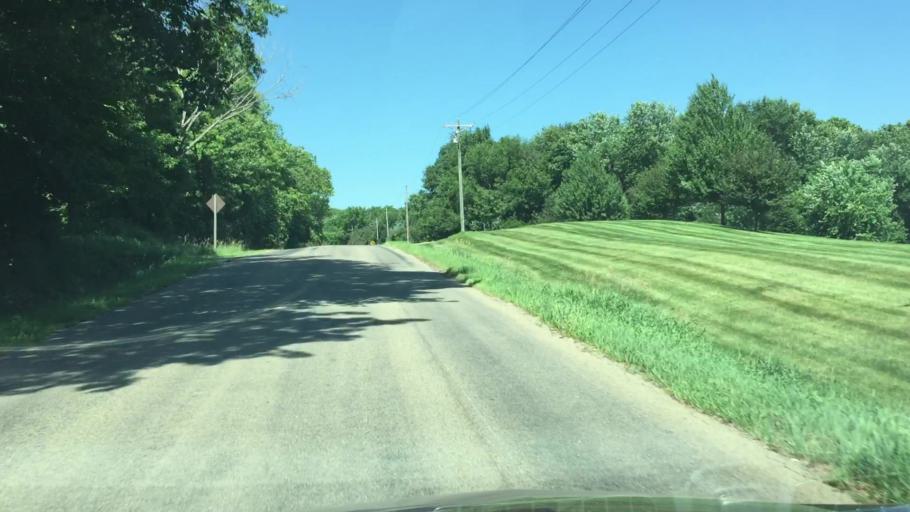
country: US
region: Iowa
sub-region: Linn County
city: Ely
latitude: 41.8156
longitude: -91.6045
